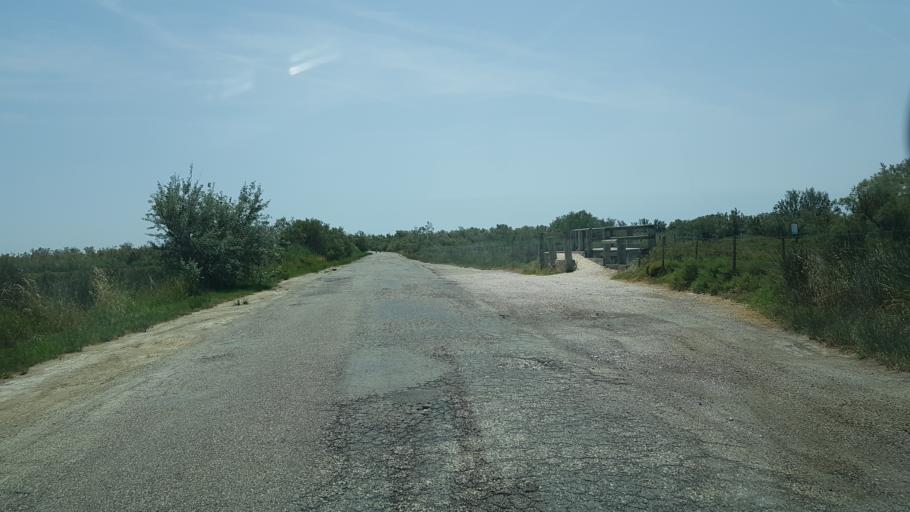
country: FR
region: Provence-Alpes-Cote d'Azur
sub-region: Departement des Bouches-du-Rhone
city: Arles
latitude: 43.5399
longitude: 4.6375
